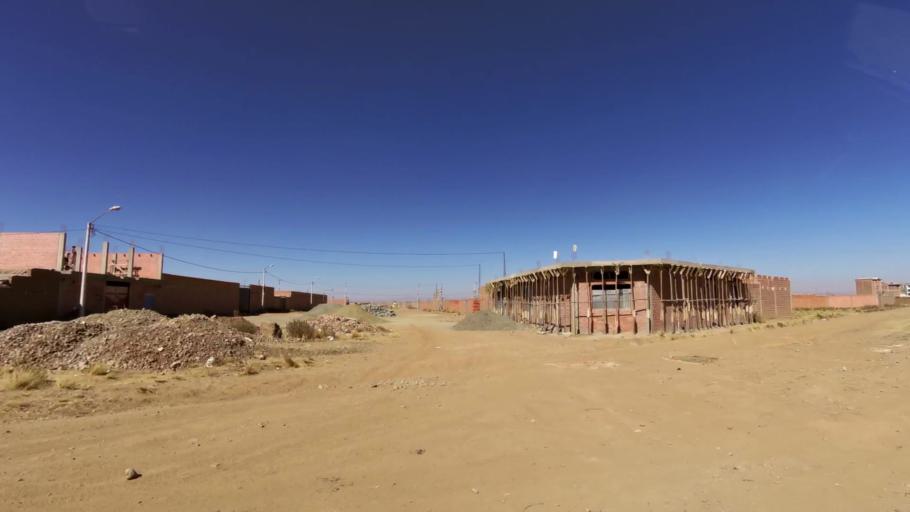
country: BO
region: La Paz
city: La Paz
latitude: -16.6165
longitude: -68.1937
